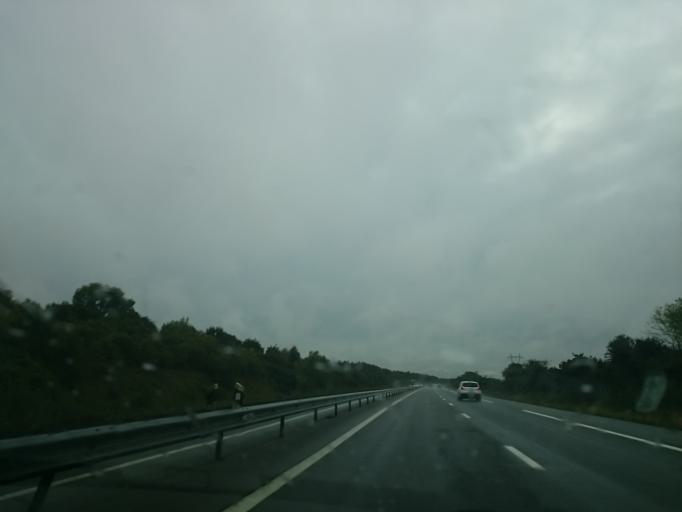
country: FR
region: Pays de la Loire
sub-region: Departement de la Loire-Atlantique
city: Prinquiau
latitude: 47.4093
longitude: -2.0169
